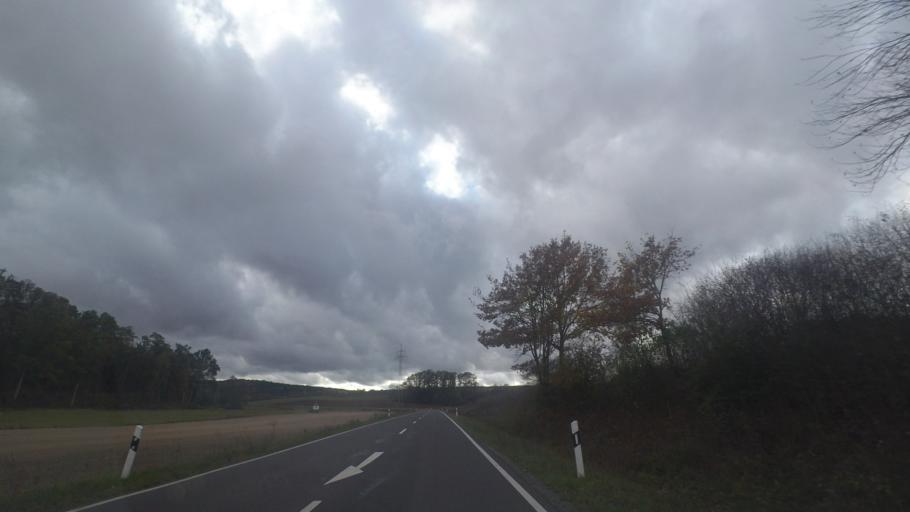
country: DE
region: Bavaria
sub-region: Regierungsbezirk Unterfranken
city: Hollstadt
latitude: 50.3301
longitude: 10.3150
